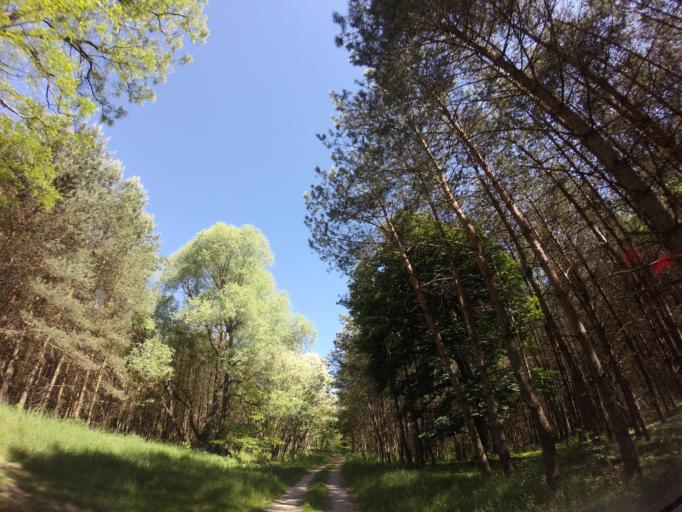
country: PL
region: West Pomeranian Voivodeship
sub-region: Powiat choszczenski
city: Drawno
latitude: 53.2772
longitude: 15.7683
